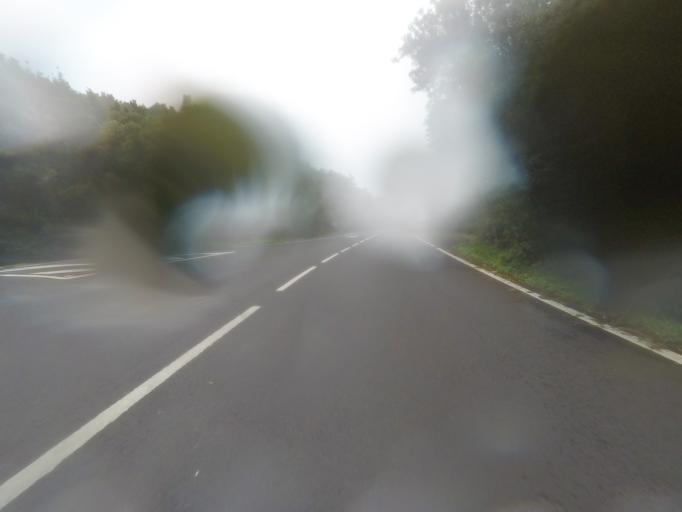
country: ES
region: Canary Islands
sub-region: Provincia de Santa Cruz de Tenerife
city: Vallehermosa
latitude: 28.1357
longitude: -17.2812
